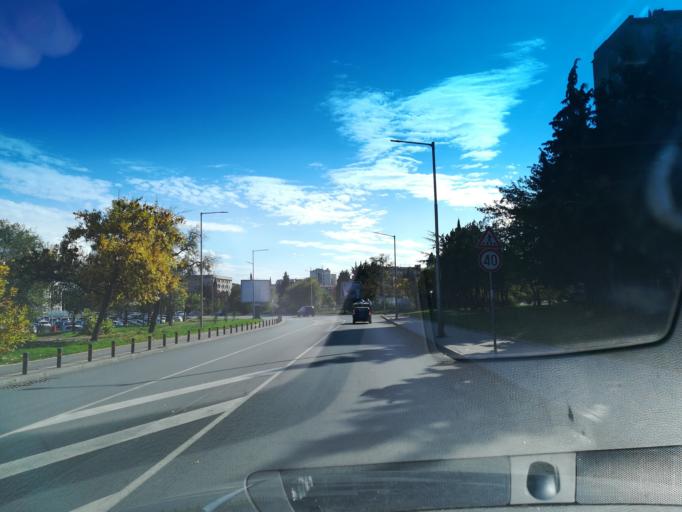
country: BG
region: Stara Zagora
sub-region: Obshtina Stara Zagora
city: Stara Zagora
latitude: 42.4333
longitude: 25.6372
